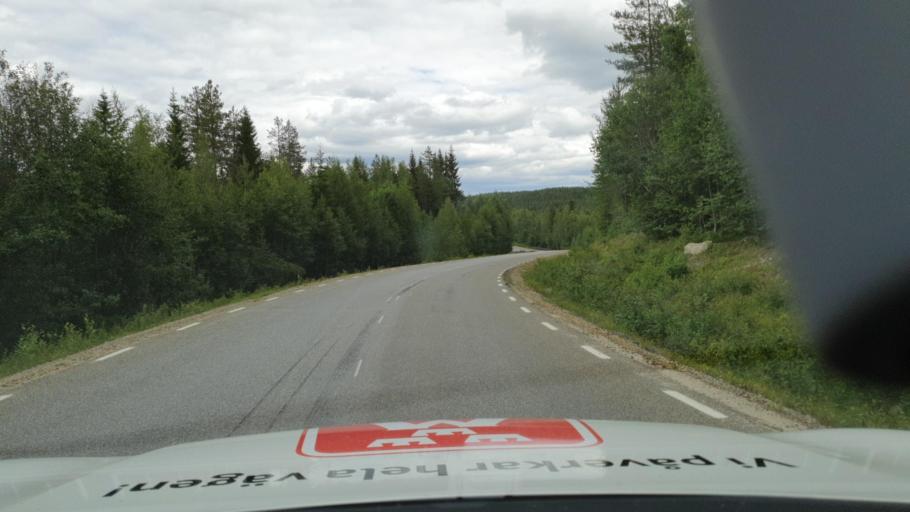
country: SE
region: Vaesterbotten
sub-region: Bjurholms Kommun
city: Bjurholm
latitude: 63.8683
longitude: 18.9714
